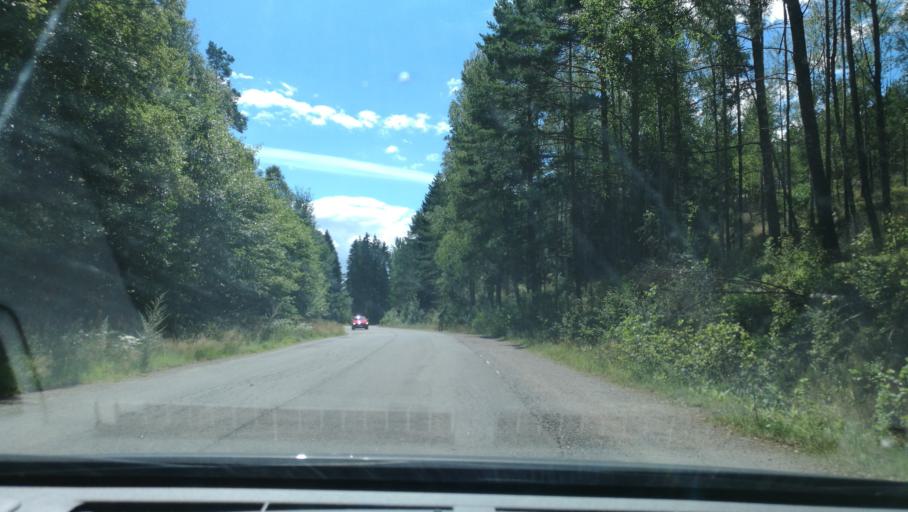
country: SE
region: OEstergoetland
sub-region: Norrkopings Kommun
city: Krokek
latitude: 58.6641
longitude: 16.4681
